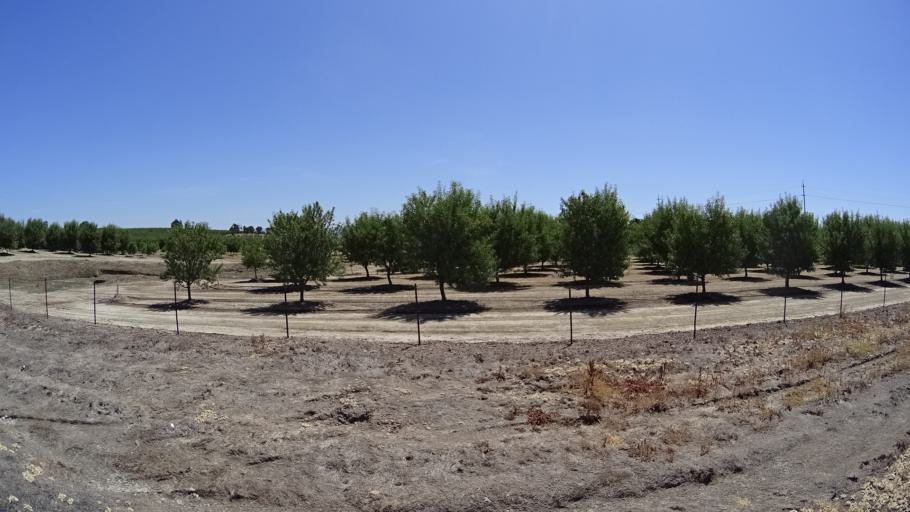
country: US
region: California
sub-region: Calaveras County
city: Rancho Calaveras
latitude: 38.0960
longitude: -120.9450
